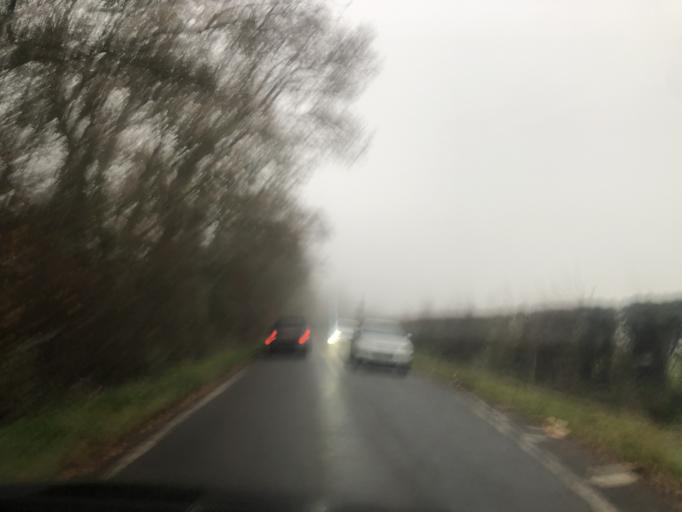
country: GB
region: England
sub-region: Oxfordshire
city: Bicester
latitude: 51.9228
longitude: -1.1864
